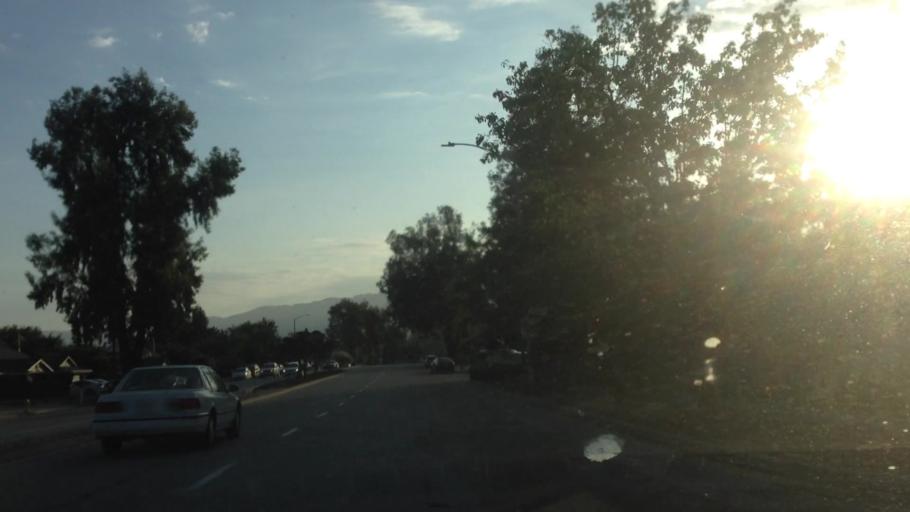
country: US
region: California
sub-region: Santa Clara County
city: Seven Trees
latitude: 37.2975
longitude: -121.8059
